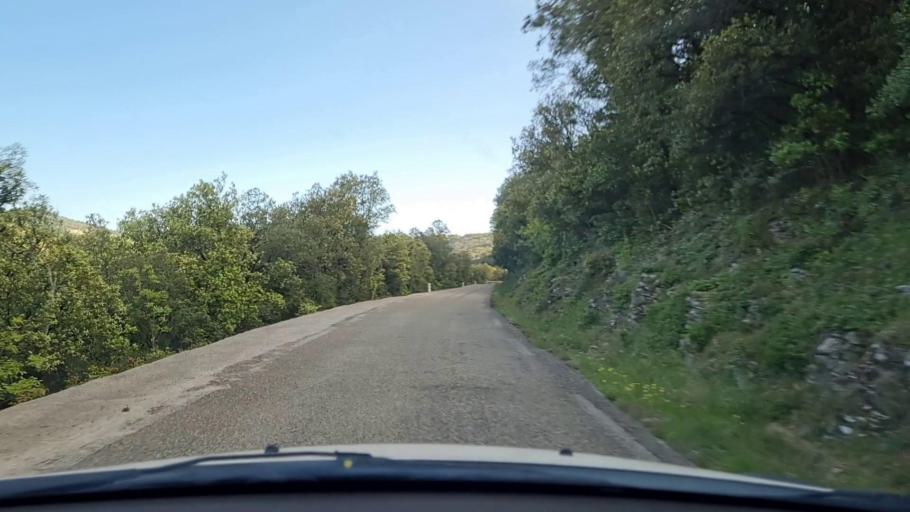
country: FR
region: Languedoc-Roussillon
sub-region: Departement du Gard
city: Les Salles-du-Gardon
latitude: 44.1696
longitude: 4.0239
